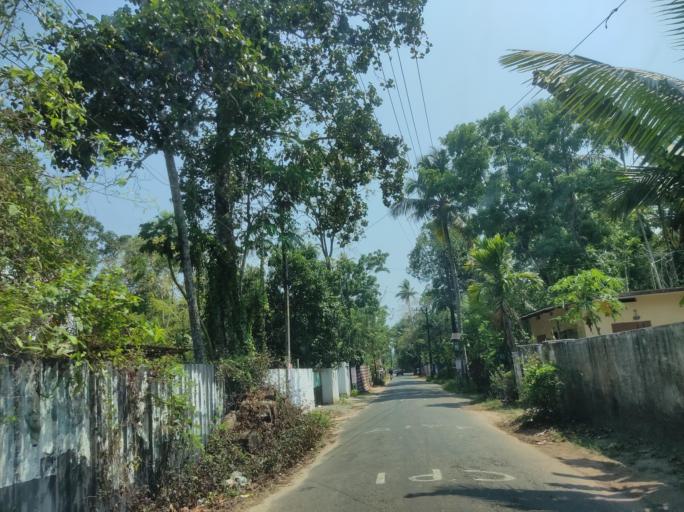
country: IN
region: Kerala
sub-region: Alappuzha
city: Vayalar
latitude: 9.6955
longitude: 76.3028
